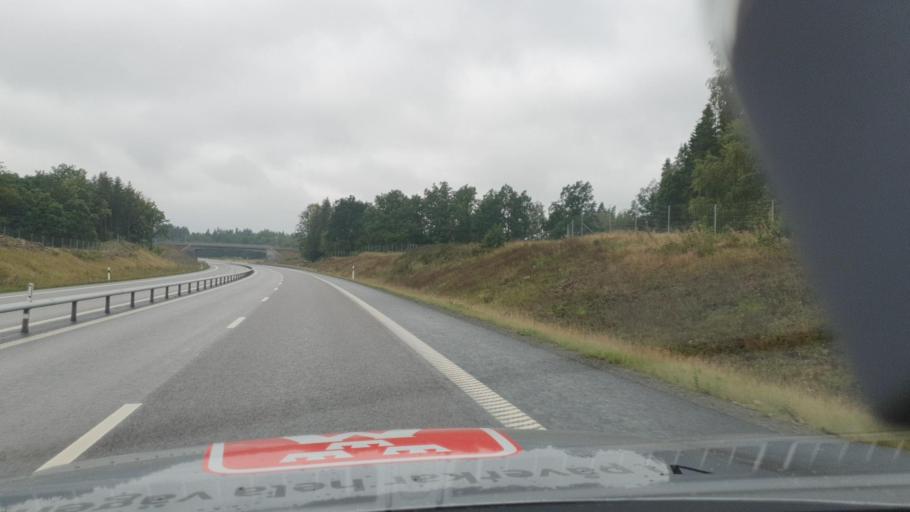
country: SE
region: Skane
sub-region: Horby Kommun
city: Hoerby
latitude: 55.9252
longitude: 13.7987
